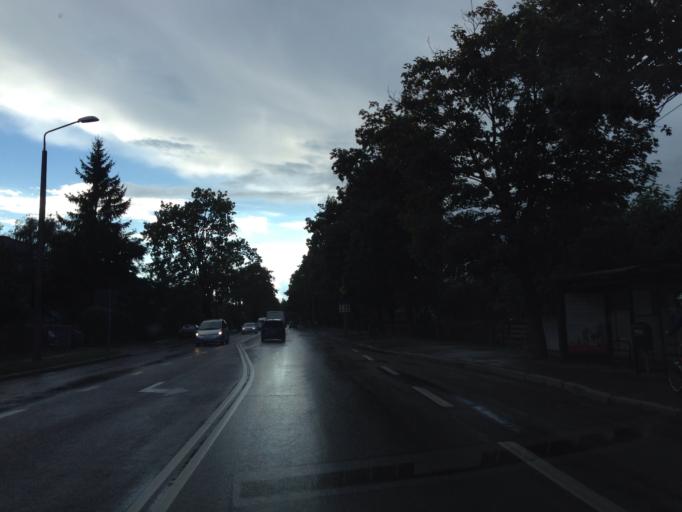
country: EE
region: Tartu
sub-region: Tartu linn
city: Tartu
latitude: 58.3639
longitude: 26.6977
